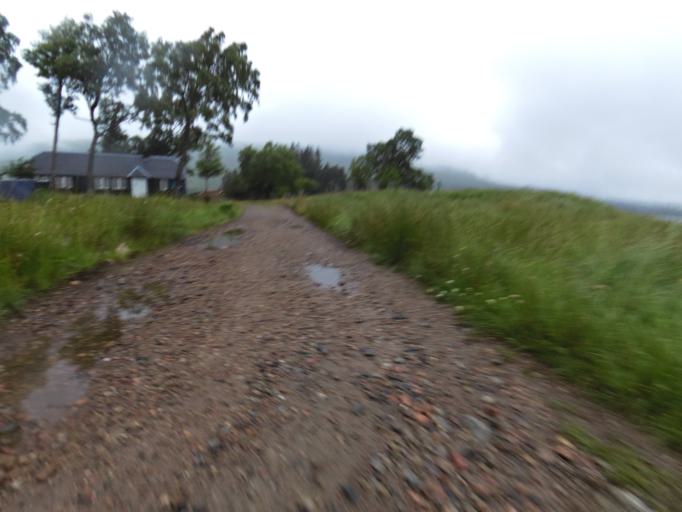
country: GB
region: Scotland
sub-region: Highland
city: Spean Bridge
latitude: 56.7664
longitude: -4.6659
